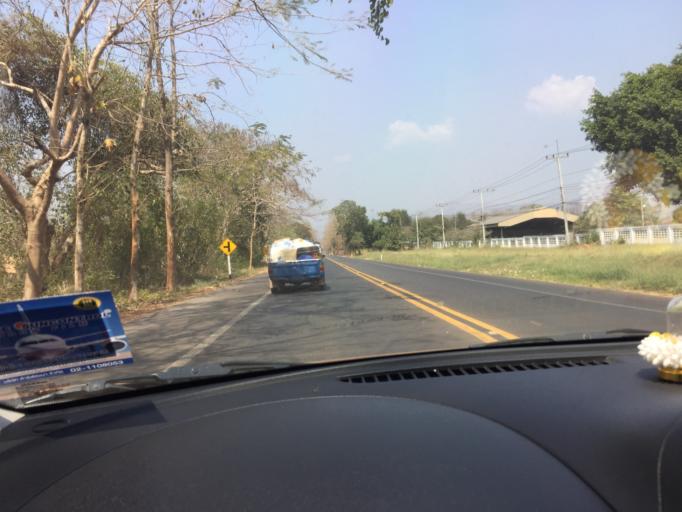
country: TH
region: Kanchanaburi
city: Sai Yok
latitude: 14.1739
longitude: 99.1292
